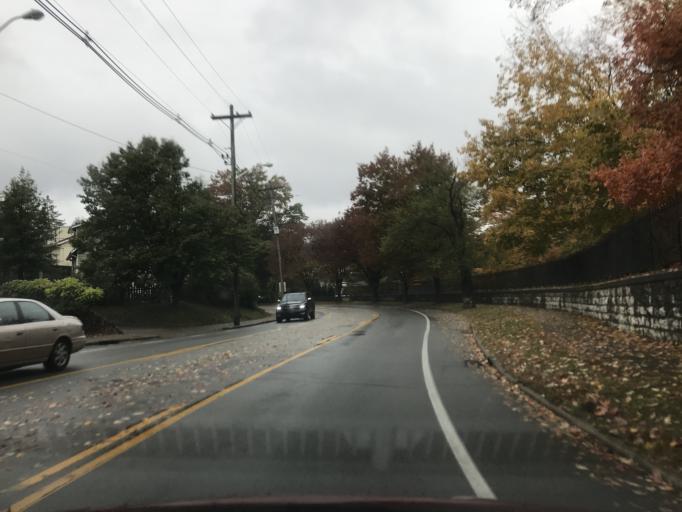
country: US
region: Kentucky
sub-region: Jefferson County
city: Audubon Park
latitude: 38.2406
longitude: -85.7155
